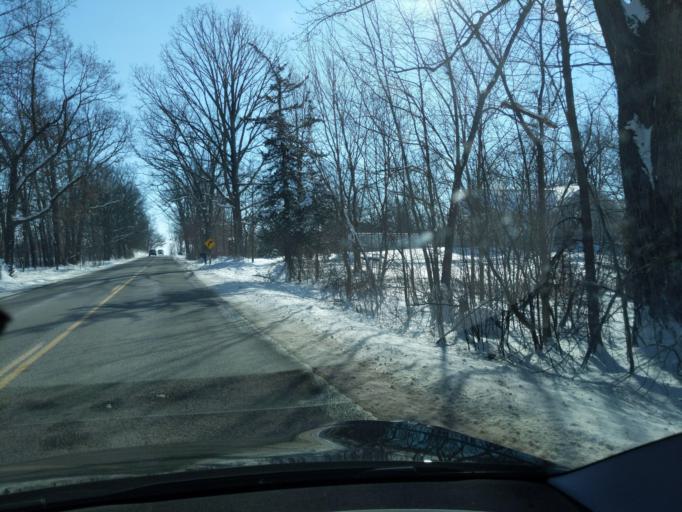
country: US
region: Michigan
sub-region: Livingston County
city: Fowlerville
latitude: 42.5710
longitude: -84.0718
